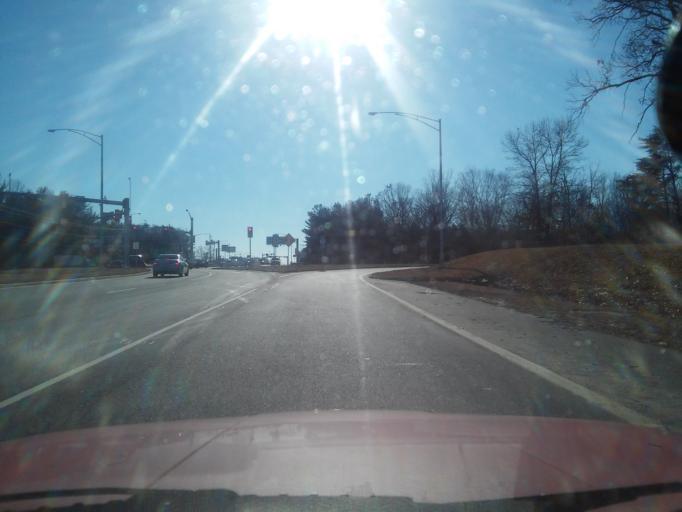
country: US
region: Virginia
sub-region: Fluvanna County
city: Palmyra
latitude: 37.9790
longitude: -78.2124
